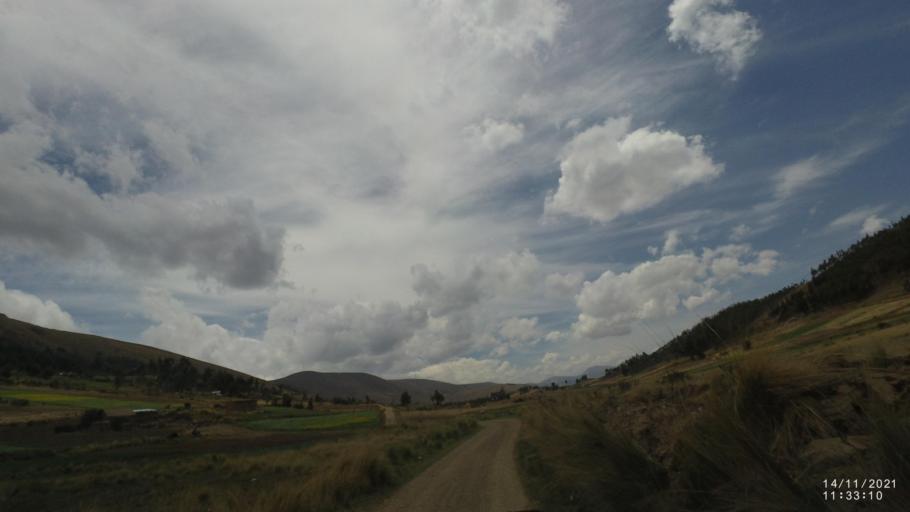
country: BO
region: Cochabamba
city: Colomi
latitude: -17.3444
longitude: -66.0080
